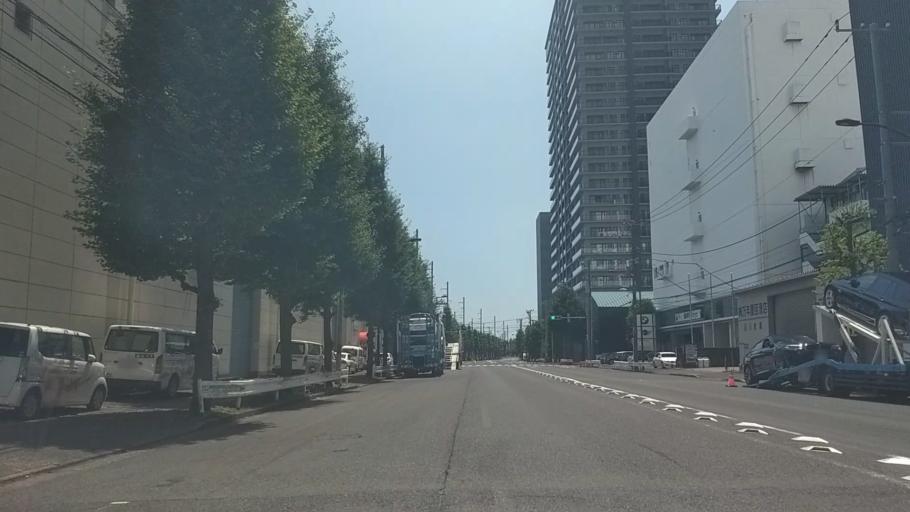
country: JP
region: Tokyo
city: Tokyo
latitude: 35.6254
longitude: 139.7542
